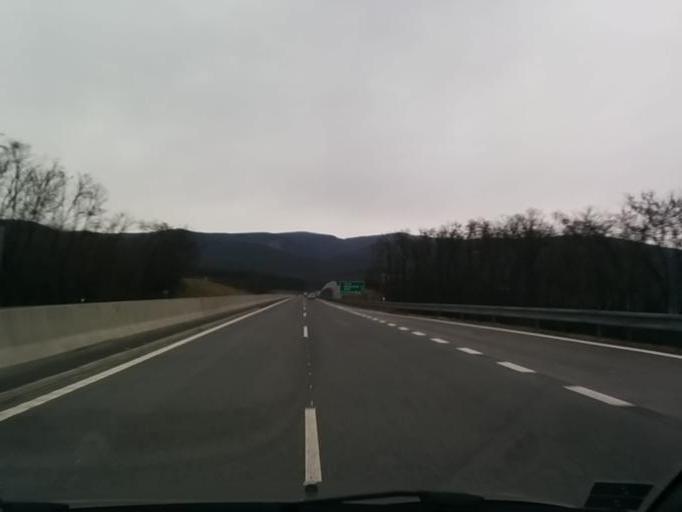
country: SK
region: Nitriansky
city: Tlmace
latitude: 48.3600
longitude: 18.4978
